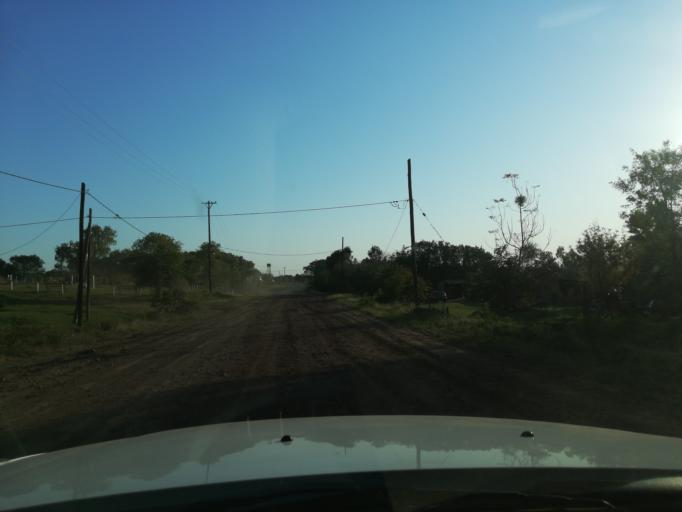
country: AR
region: Misiones
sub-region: Departamento de Apostoles
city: San Jose
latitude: -27.6314
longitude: -55.7283
